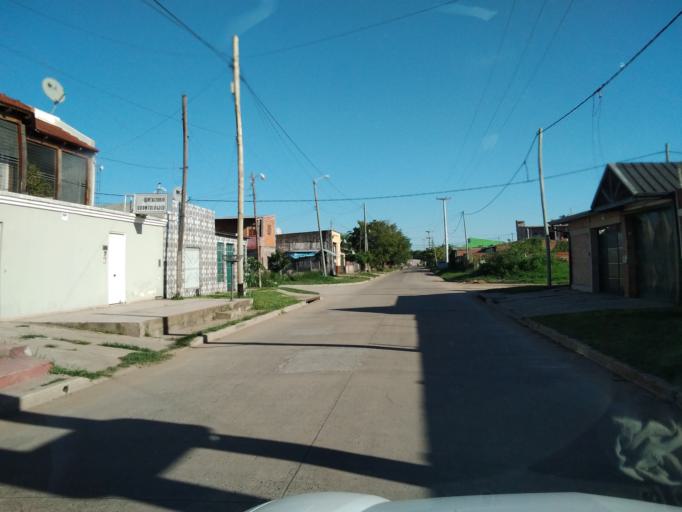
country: AR
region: Corrientes
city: Corrientes
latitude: -27.4715
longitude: -58.7915
